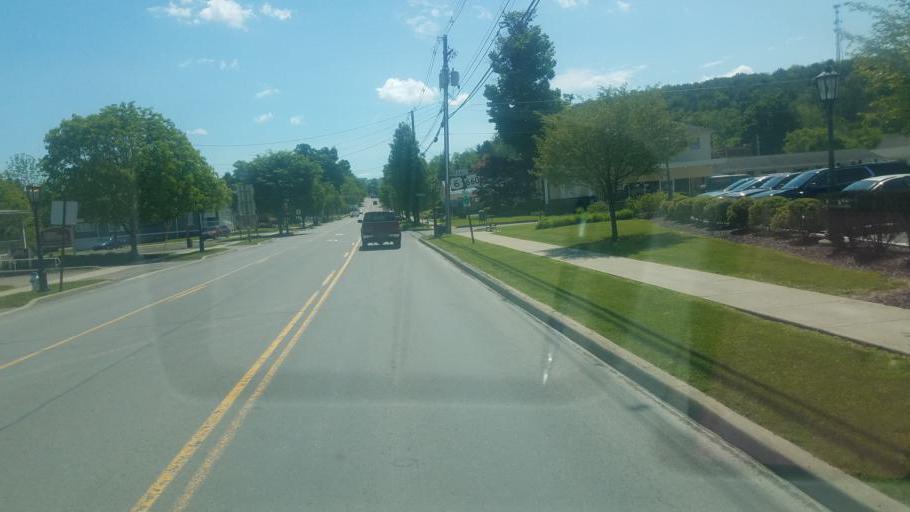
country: US
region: Pennsylvania
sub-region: Tioga County
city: Wellsboro
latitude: 41.7488
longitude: -77.2981
